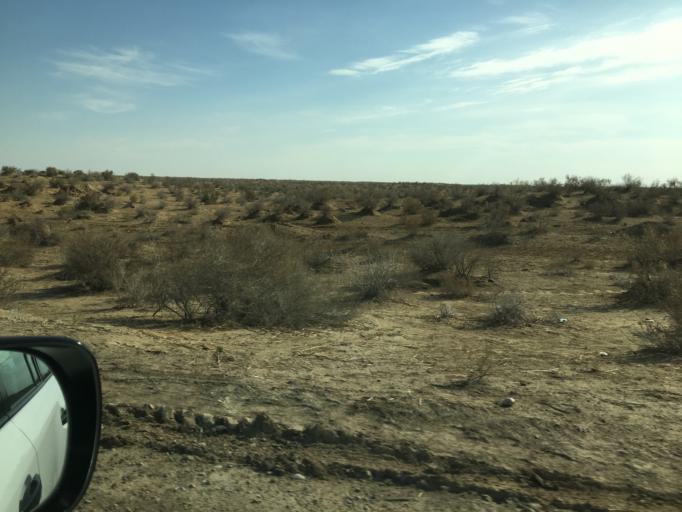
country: TM
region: Mary
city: Mary
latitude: 37.5452
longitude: 61.4269
